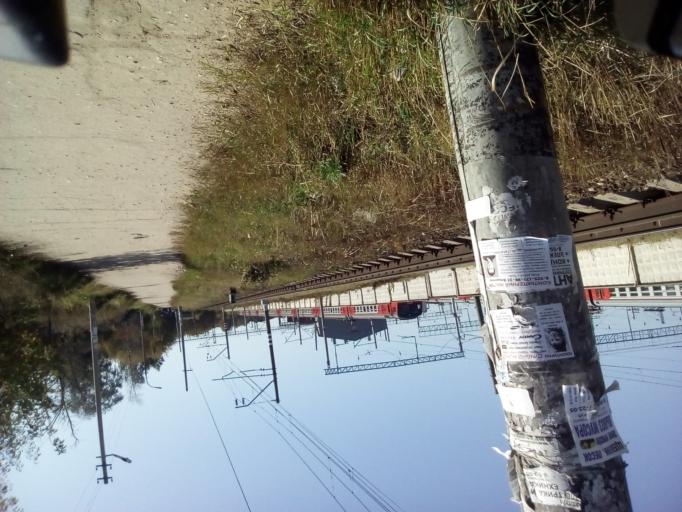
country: RU
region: Moskovskaya
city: Ramenskoye
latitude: 55.5580
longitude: 38.2446
